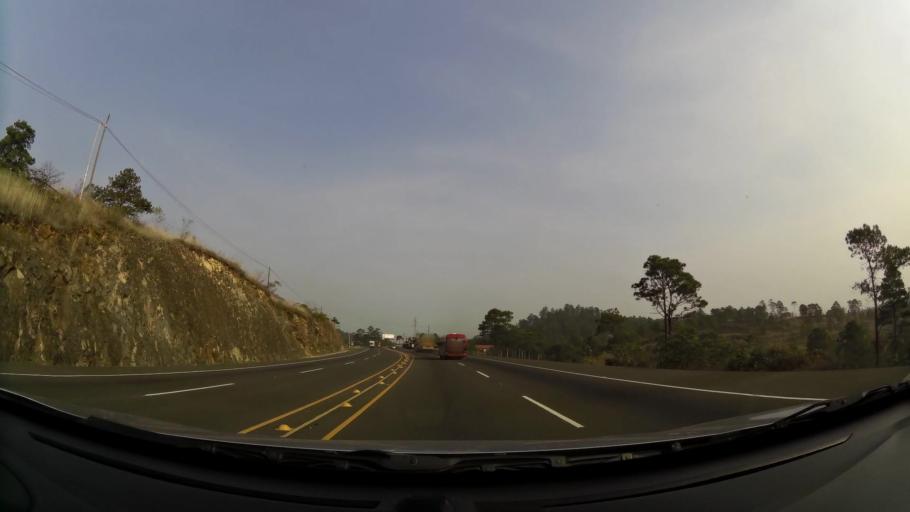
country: HN
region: Francisco Morazan
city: Zambrano
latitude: 14.2644
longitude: -87.3934
